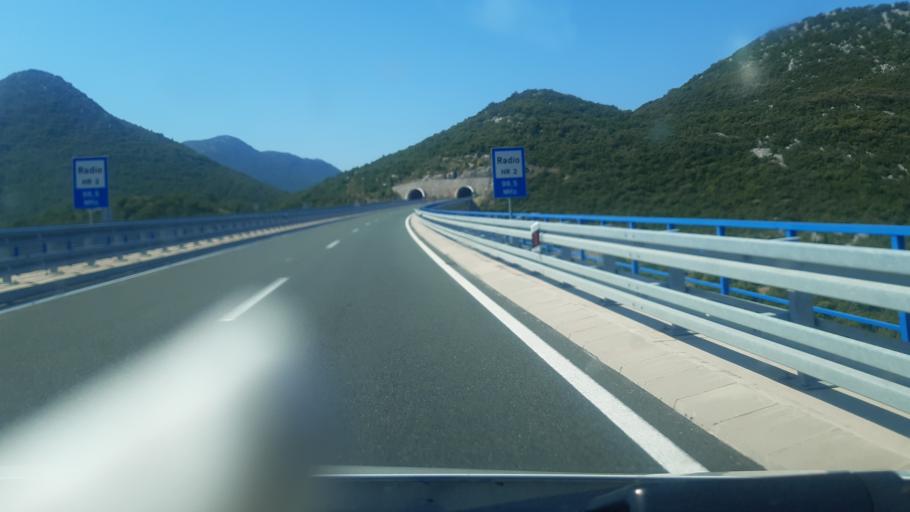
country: HR
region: Dubrovacko-Neretvanska
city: Komin
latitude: 43.1191
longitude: 17.4834
